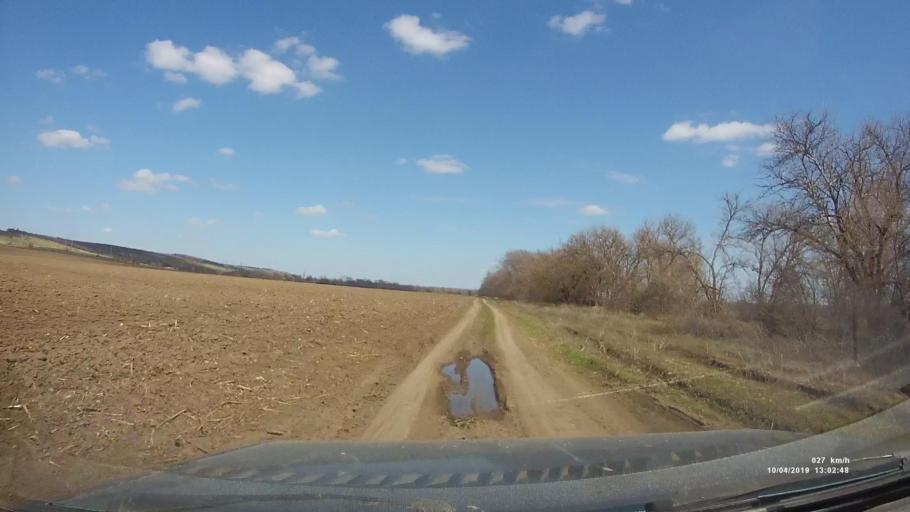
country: RU
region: Rostov
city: Masalovka
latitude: 48.3822
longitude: 40.2318
